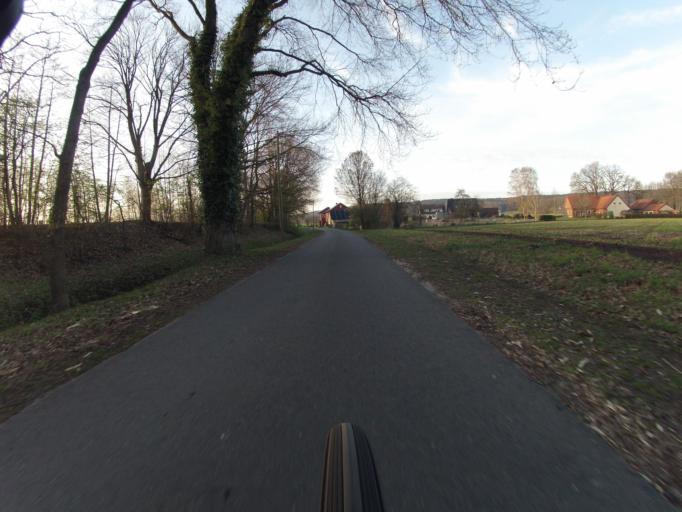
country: DE
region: North Rhine-Westphalia
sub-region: Regierungsbezirk Munster
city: Birgte
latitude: 52.2420
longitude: 7.6725
